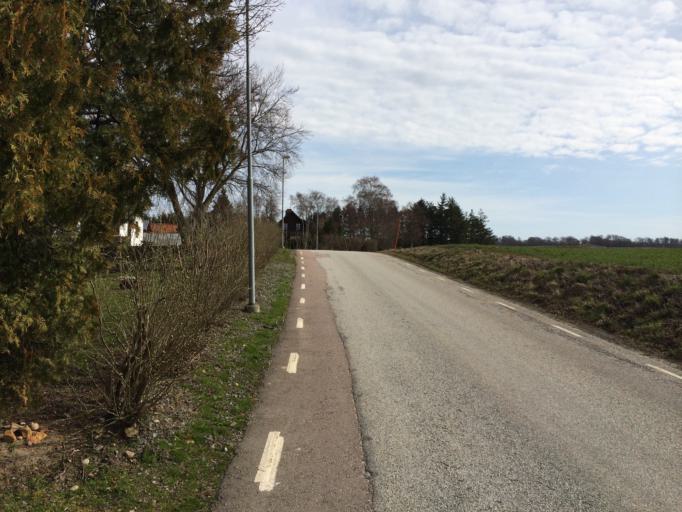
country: SE
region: Skane
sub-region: Ystads Kommun
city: Ystad
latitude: 55.4621
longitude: 13.7528
